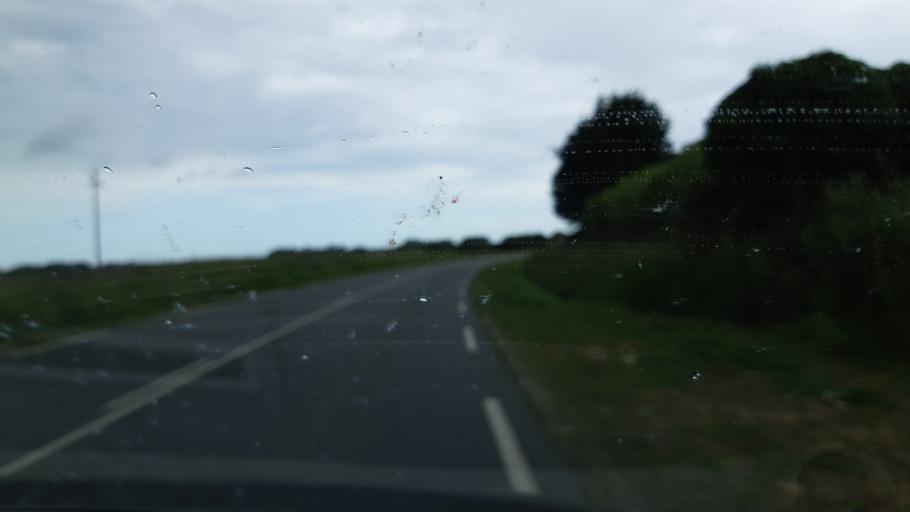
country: FR
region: Brittany
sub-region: Departement du Finistere
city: Plougoulm
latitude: 48.6330
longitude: -4.0549
